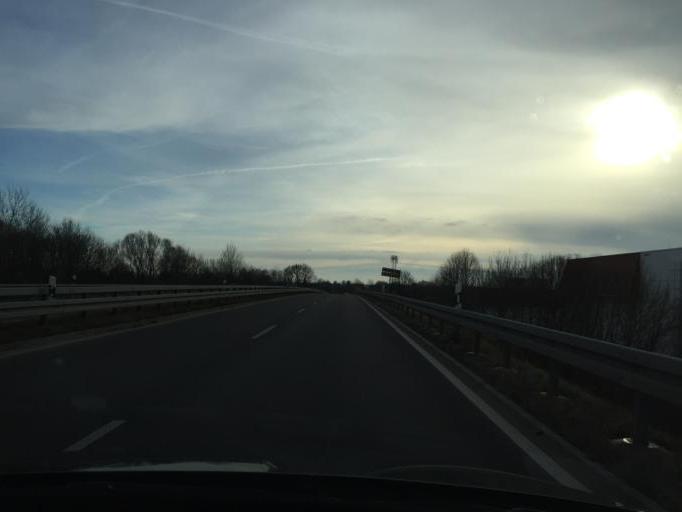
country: DE
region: Brandenburg
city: Peitz
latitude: 51.8168
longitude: 14.3874
